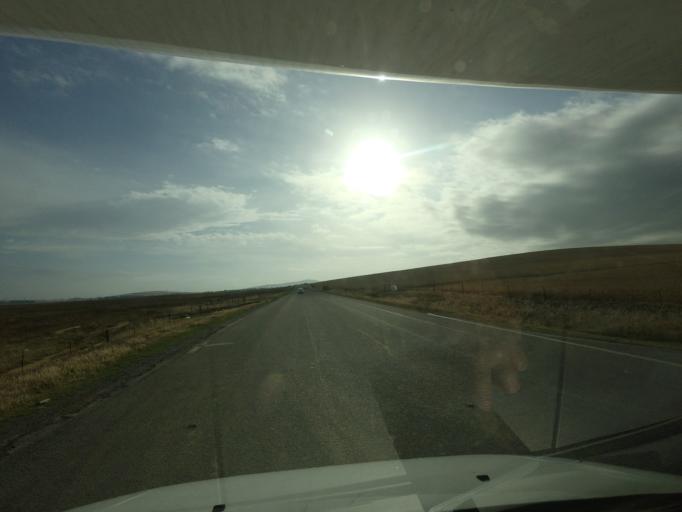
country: ZA
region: Western Cape
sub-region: City of Cape Town
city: Sunset Beach
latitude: -33.7254
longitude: 18.4899
